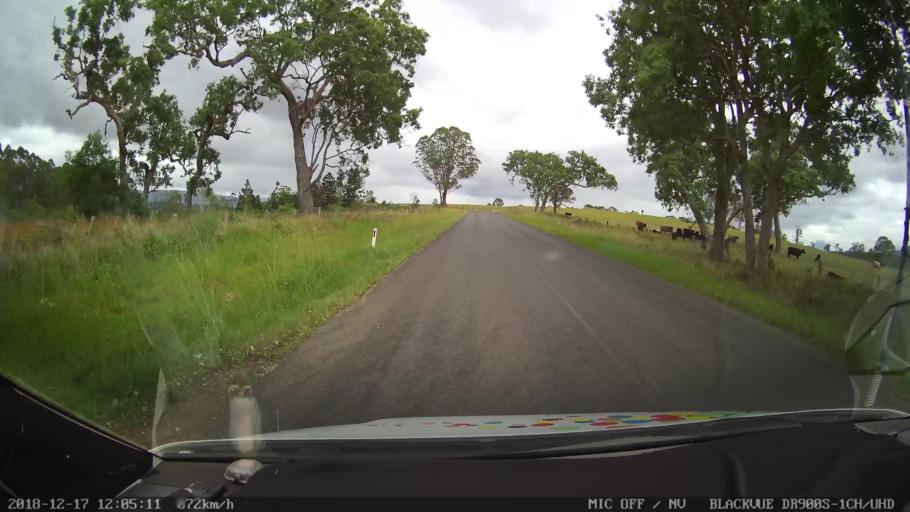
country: AU
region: New South Wales
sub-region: Kyogle
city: Kyogle
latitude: -28.4949
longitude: 152.5673
